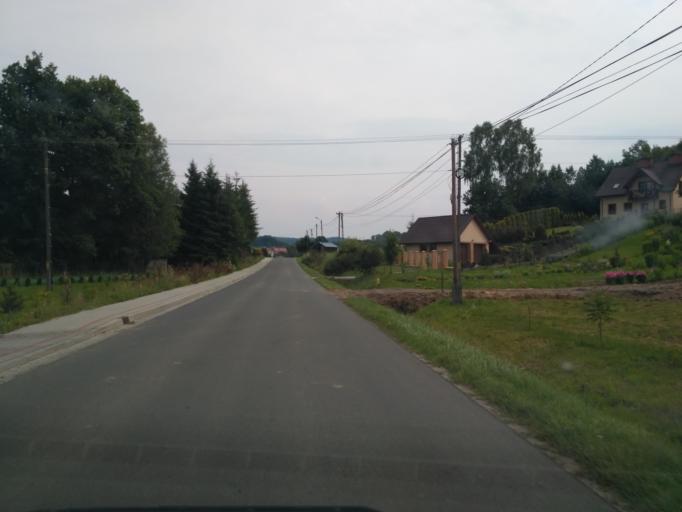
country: PL
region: Subcarpathian Voivodeship
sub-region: Powiat strzyzowski
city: Konieczkowa
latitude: 49.8480
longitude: 21.9169
